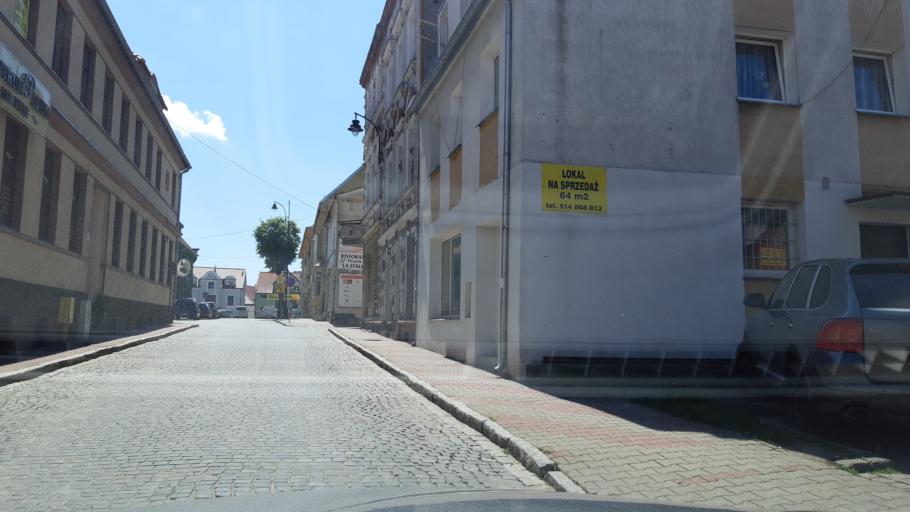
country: PL
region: Warmian-Masurian Voivodeship
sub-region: Powiat mragowski
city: Mragowo
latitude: 53.8711
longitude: 21.3034
